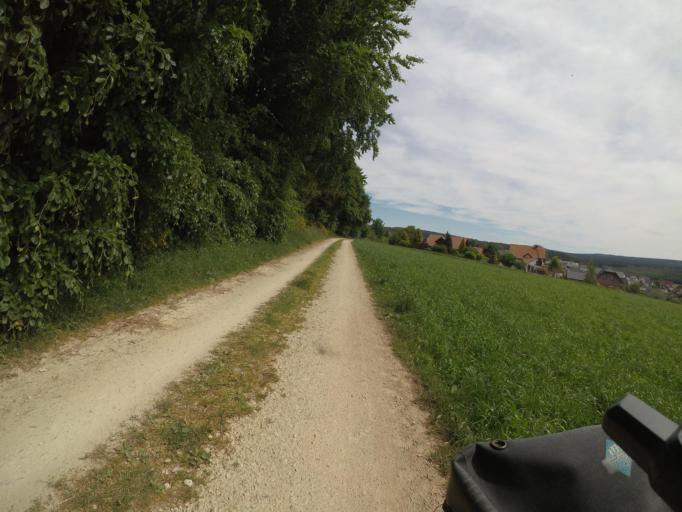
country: DE
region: Rheinland-Pfalz
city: Damflos
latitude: 49.6859
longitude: 6.9770
